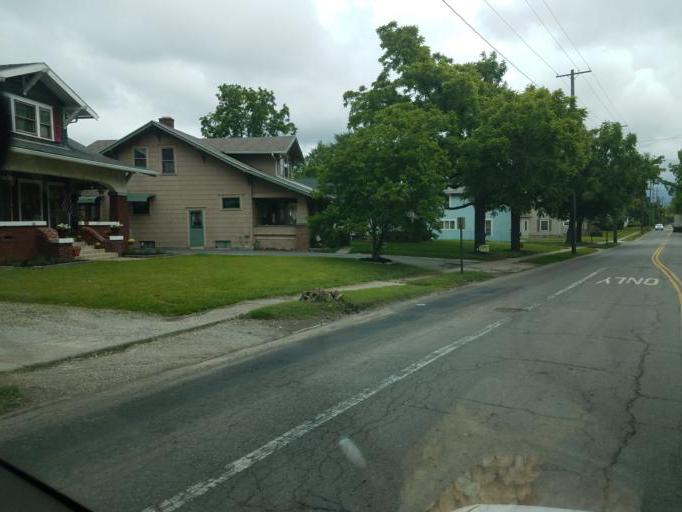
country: US
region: Ohio
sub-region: Marion County
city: Marion
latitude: 40.5744
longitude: -83.1328
